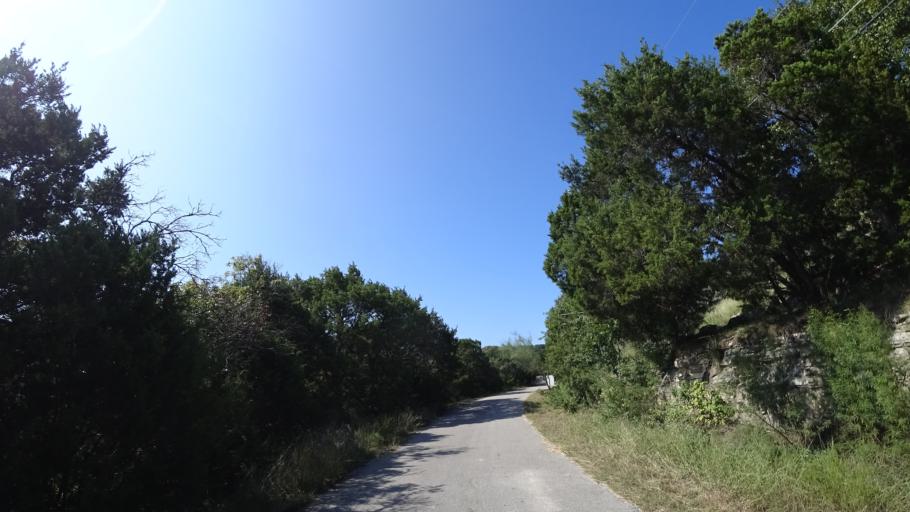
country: US
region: Texas
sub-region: Travis County
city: West Lake Hills
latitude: 30.2954
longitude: -97.8084
